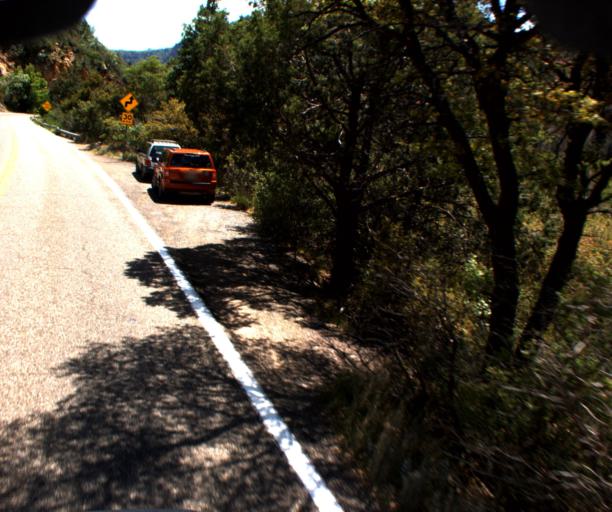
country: US
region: Arizona
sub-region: Coconino County
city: Sedona
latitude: 34.9551
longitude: -111.7546
